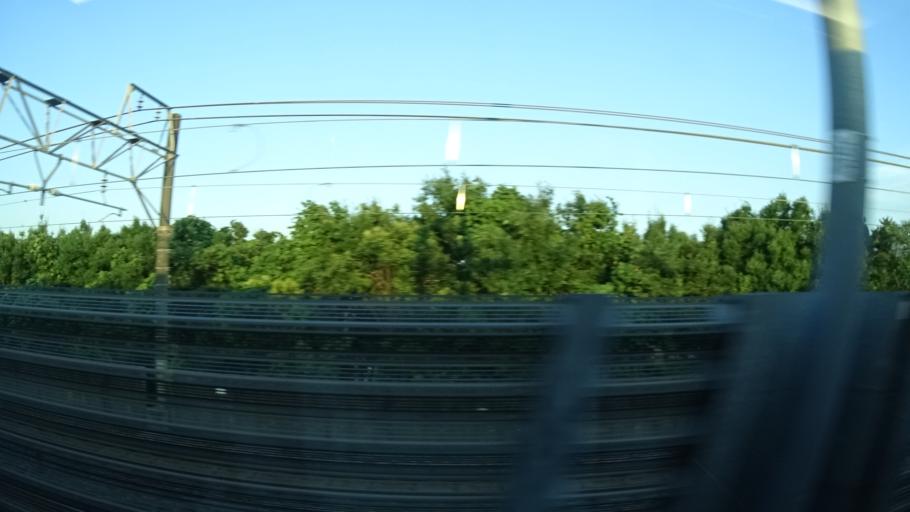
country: JP
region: Ibaraki
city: Toride
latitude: 35.8816
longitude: 140.0540
